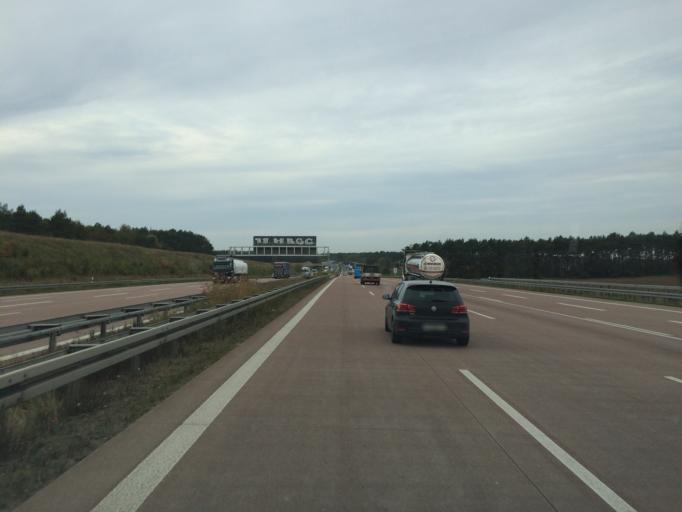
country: DE
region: Brandenburg
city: Michendorf
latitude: 52.3008
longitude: 13.0615
